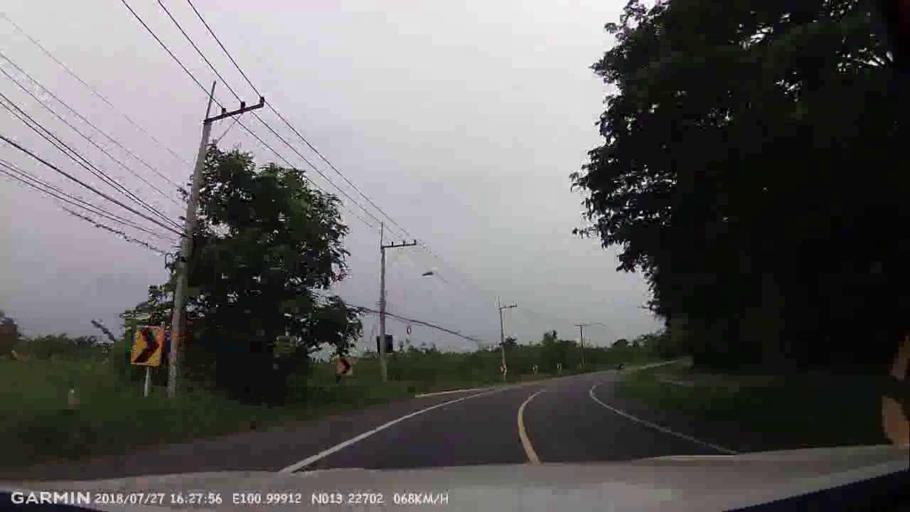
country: TH
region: Chon Buri
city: Si Racha
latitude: 13.2269
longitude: 100.9992
